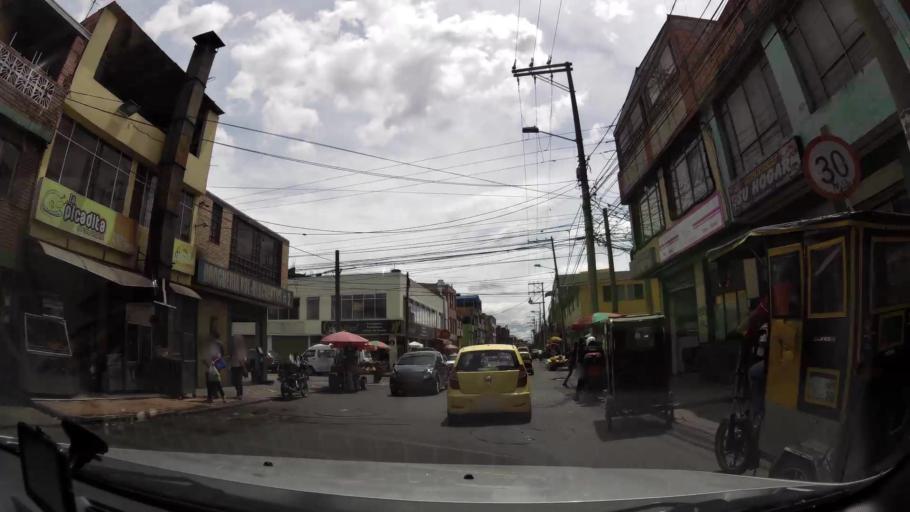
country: CO
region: Bogota D.C.
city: Bogota
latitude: 4.6406
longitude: -74.1591
